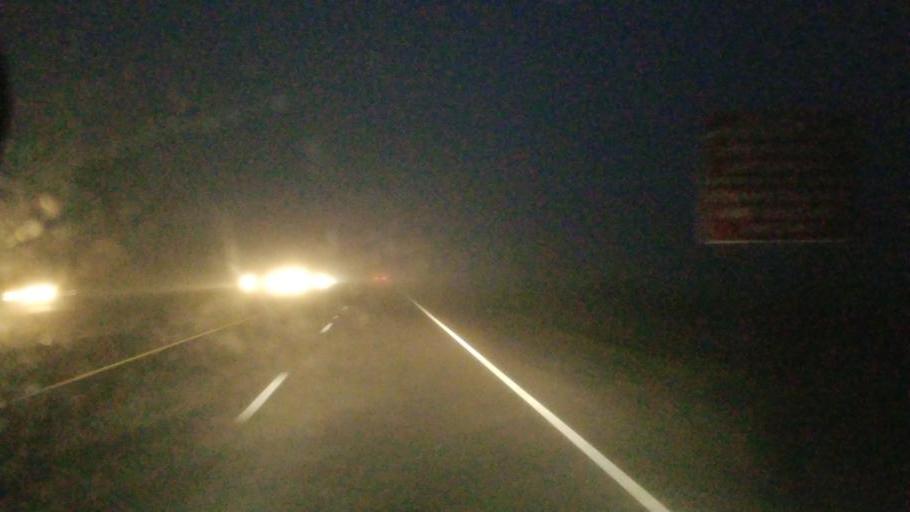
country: US
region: Ohio
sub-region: Ross County
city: Kingston
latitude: 39.4306
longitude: -82.9753
